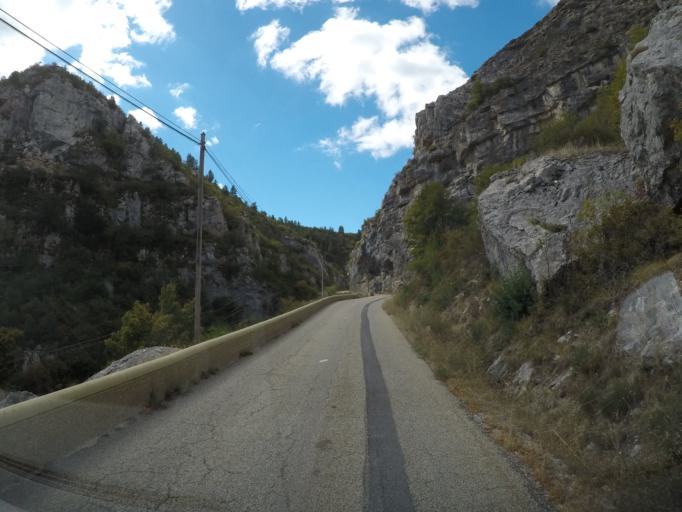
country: FR
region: Provence-Alpes-Cote d'Azur
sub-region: Departement des Hautes-Alpes
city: Laragne-Monteglin
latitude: 44.1724
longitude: 5.6367
